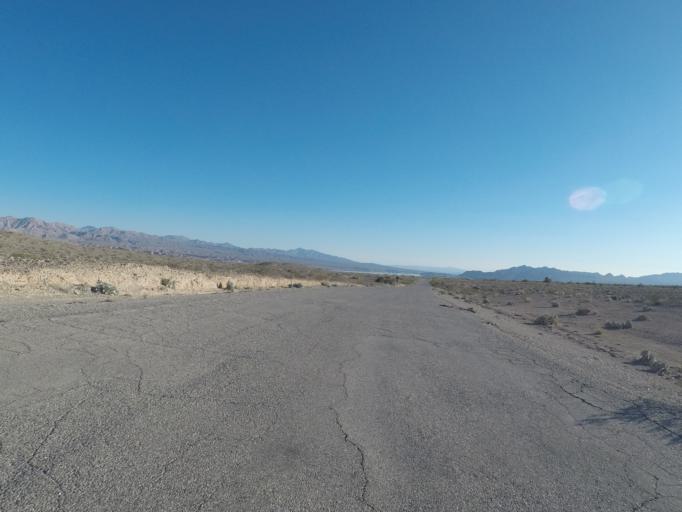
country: US
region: Nevada
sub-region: Clark County
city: Moapa Valley
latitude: 36.3933
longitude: -114.4232
